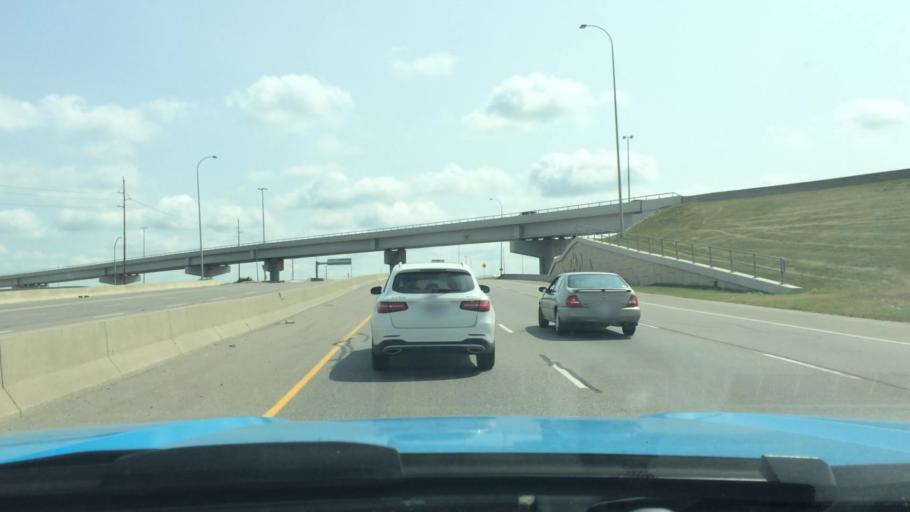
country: CA
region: Alberta
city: Calgary
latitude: 51.0957
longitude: -113.9853
